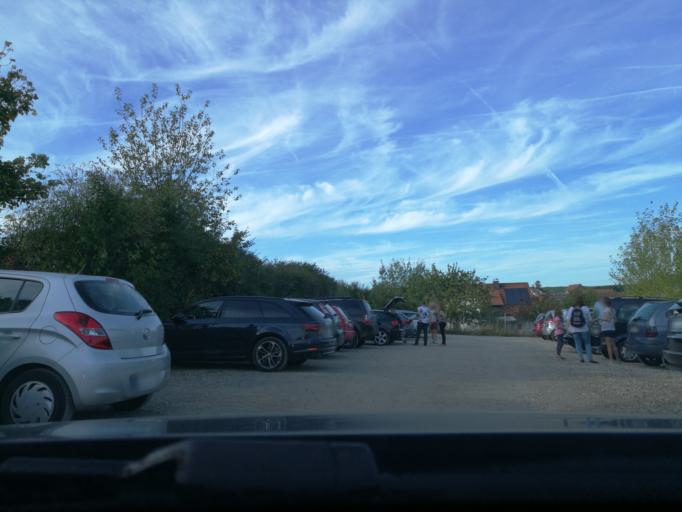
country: DE
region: Bavaria
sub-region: Regierungsbezirk Mittelfranken
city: Weisendorf
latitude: 49.5917
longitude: 10.8480
